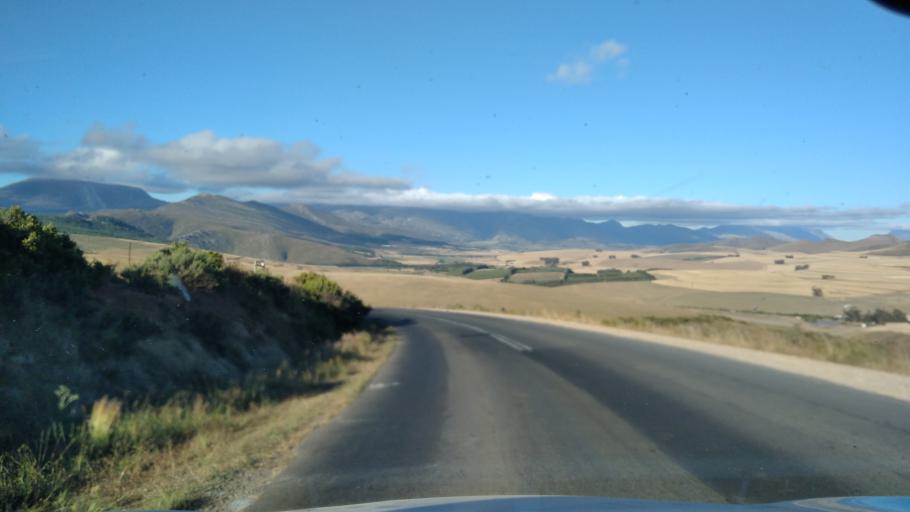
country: ZA
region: Western Cape
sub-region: Overberg District Municipality
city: Caledon
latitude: -34.1270
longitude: 19.2968
